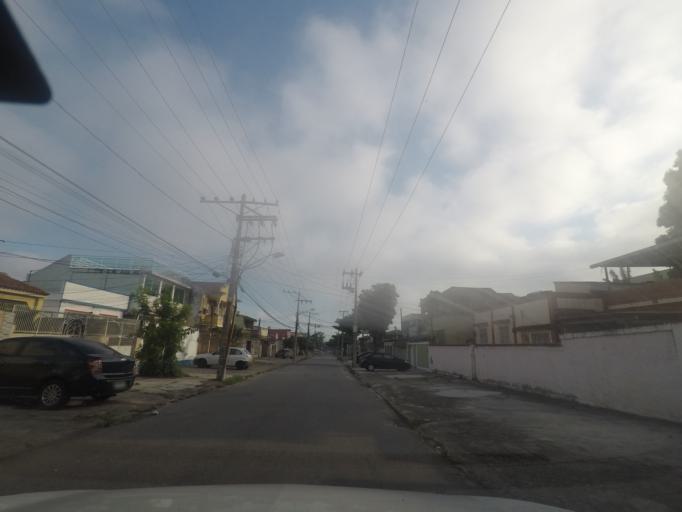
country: BR
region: Rio de Janeiro
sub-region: Duque De Caxias
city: Duque de Caxias
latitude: -22.8410
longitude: -43.2741
